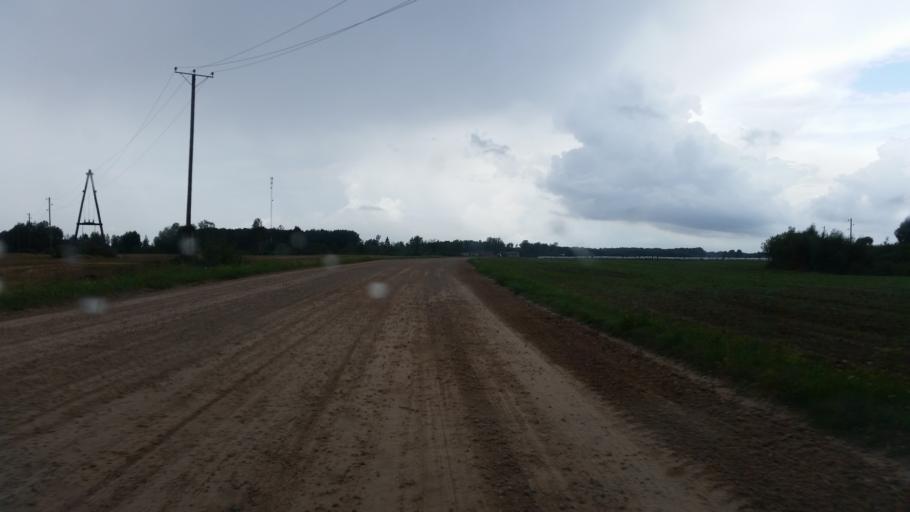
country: LV
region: Vecumnieki
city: Vecumnieki
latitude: 56.4260
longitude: 24.4774
